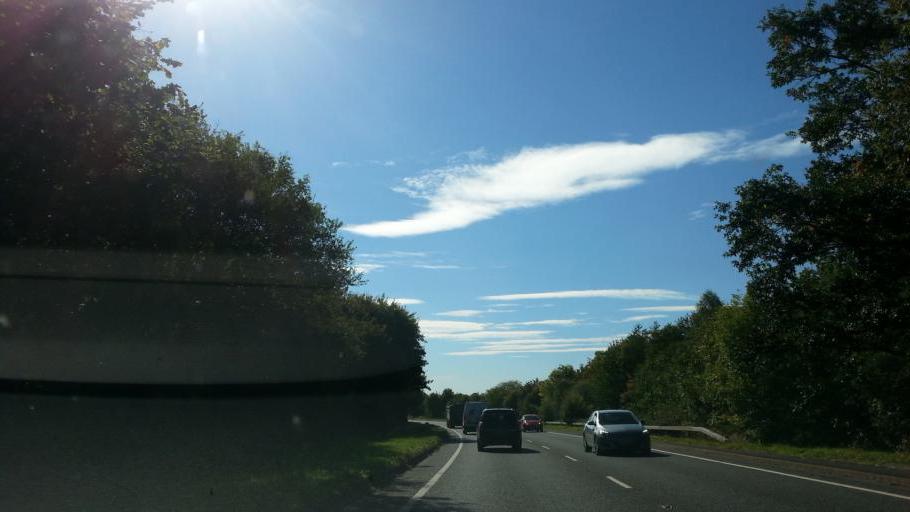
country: GB
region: England
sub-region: Telford and Wrekin
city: Chetwynd
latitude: 52.7499
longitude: -2.3941
